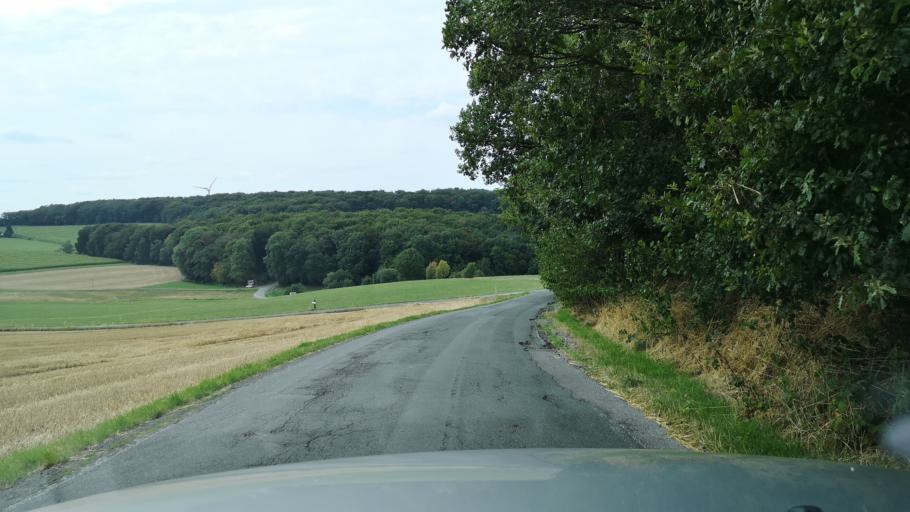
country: DE
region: North Rhine-Westphalia
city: Sprockhovel
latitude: 51.3386
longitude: 7.2105
